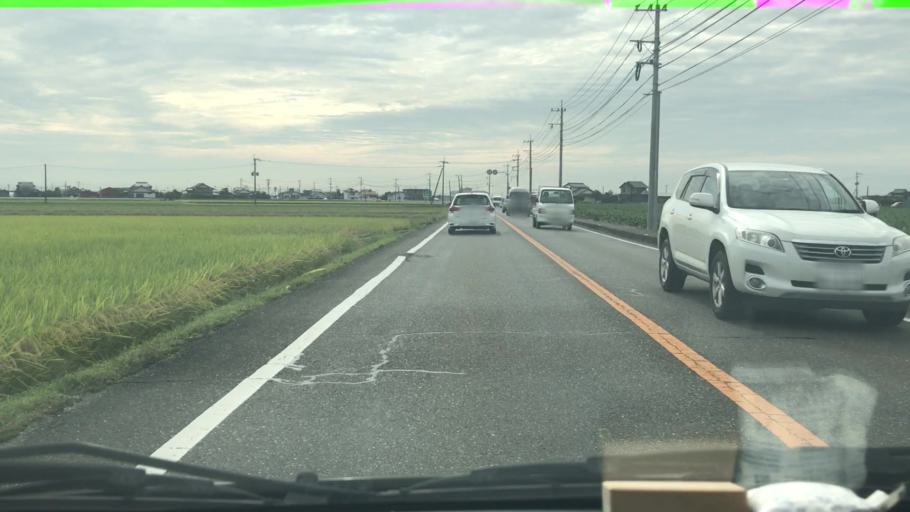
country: JP
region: Saga Prefecture
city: Takeocho-takeo
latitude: 33.2012
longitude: 130.0967
